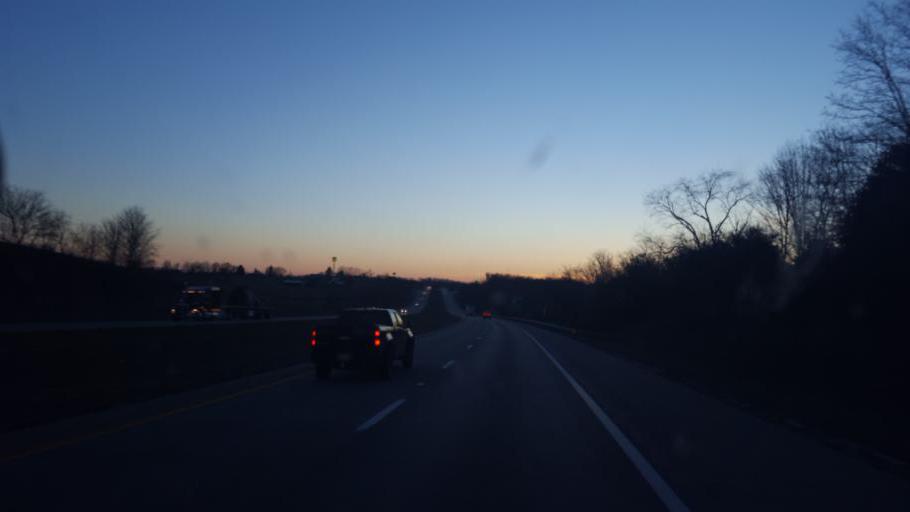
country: US
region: Ohio
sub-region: Belmont County
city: Bethesda
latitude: 40.0646
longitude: -81.0391
